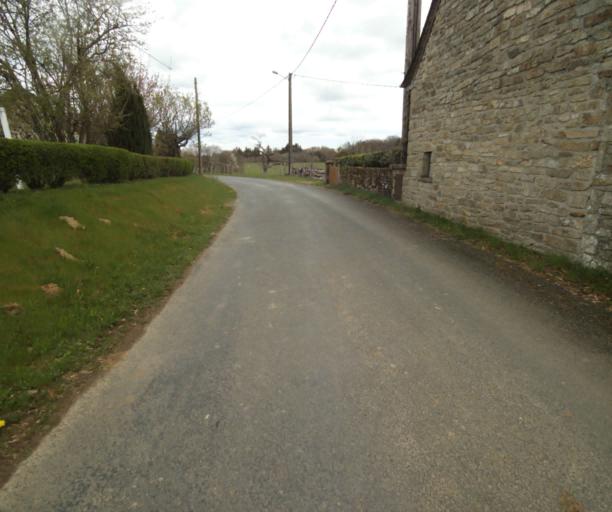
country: FR
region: Limousin
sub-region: Departement de la Correze
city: Laguenne
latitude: 45.2040
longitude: 1.8813
